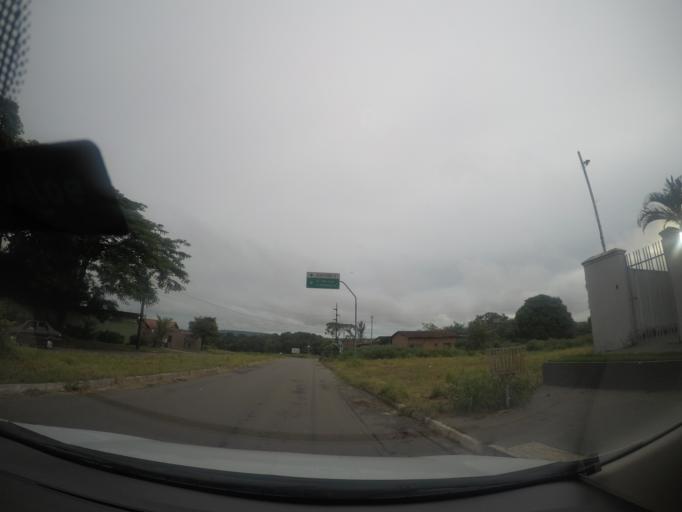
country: BR
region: Goias
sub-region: Goiania
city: Goiania
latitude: -16.7552
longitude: -49.3127
